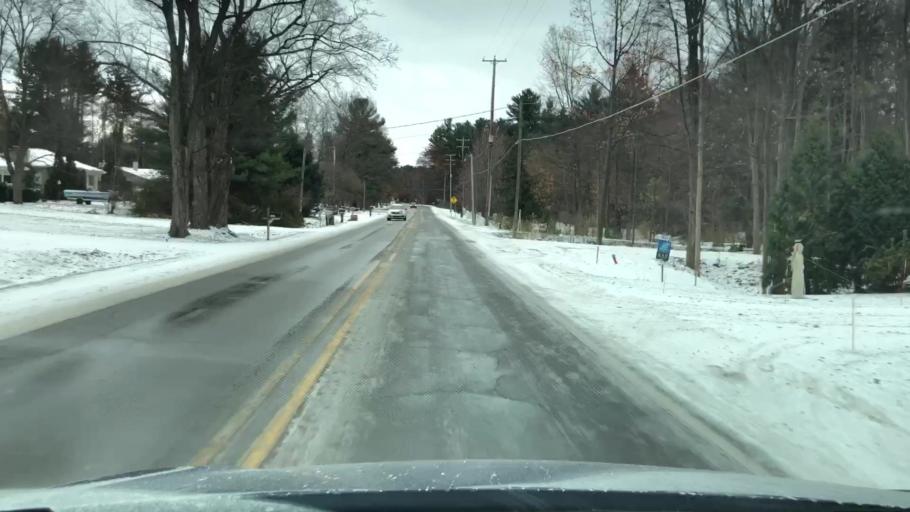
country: US
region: Michigan
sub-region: Grand Traverse County
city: Traverse City
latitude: 44.7769
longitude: -85.5909
